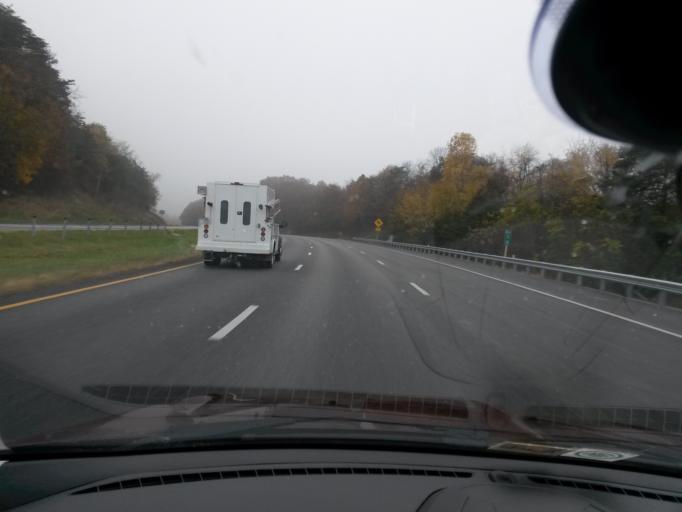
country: US
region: Virginia
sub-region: City of Covington
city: Fairlawn
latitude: 37.7763
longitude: -79.9769
